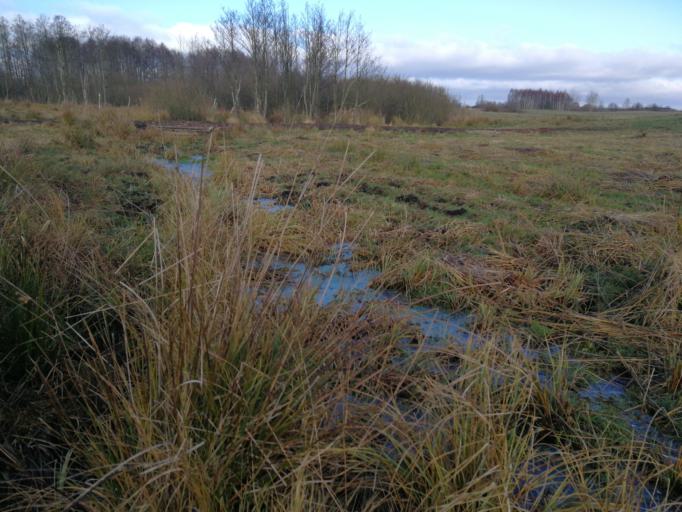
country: PL
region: Warmian-Masurian Voivodeship
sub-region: Powiat dzialdowski
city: Rybno
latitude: 53.4114
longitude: 19.9114
